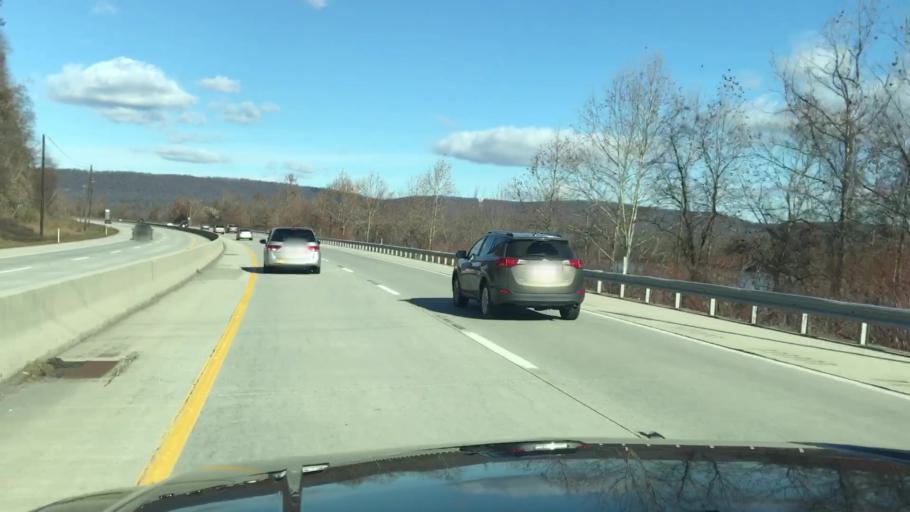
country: US
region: Pennsylvania
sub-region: Dauphin County
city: Matamoras
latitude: 40.4821
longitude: -76.9491
